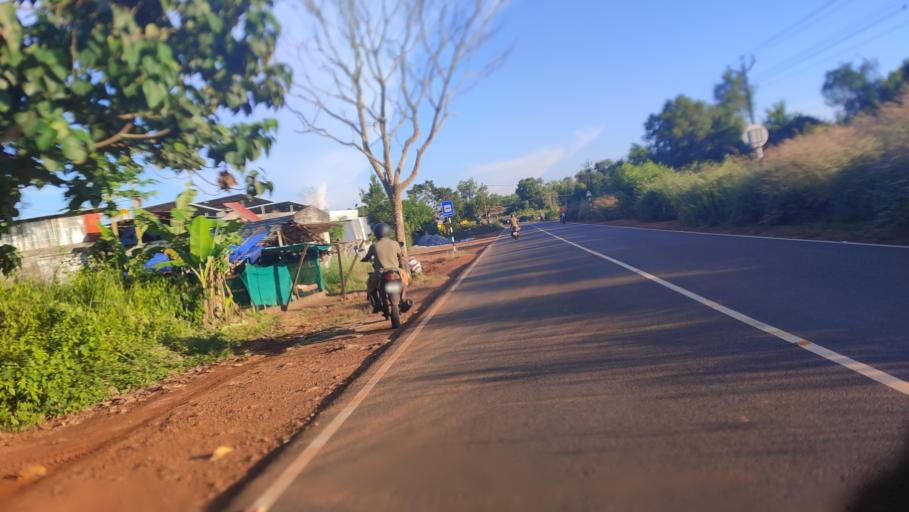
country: IN
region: Kerala
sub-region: Kasaragod District
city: Kasaragod
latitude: 12.4653
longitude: 75.0647
